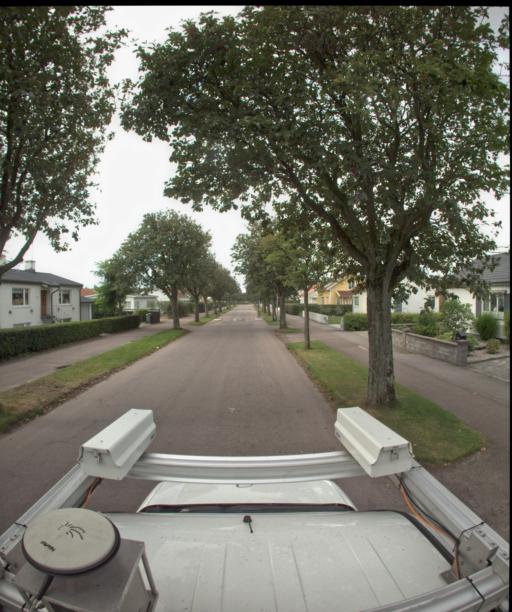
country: SE
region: Halland
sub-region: Falkenbergs Kommun
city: Falkenberg
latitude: 56.8905
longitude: 12.5006
